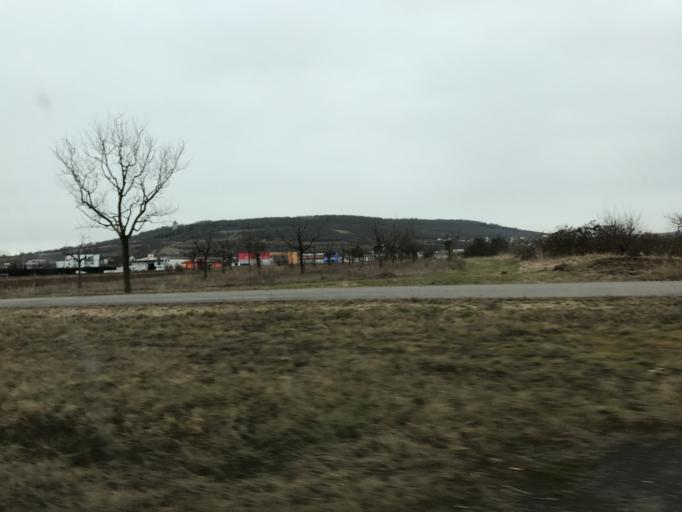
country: DE
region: Rheinland-Pfalz
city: Gau-Algesheim
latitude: 49.9707
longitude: 8.0169
